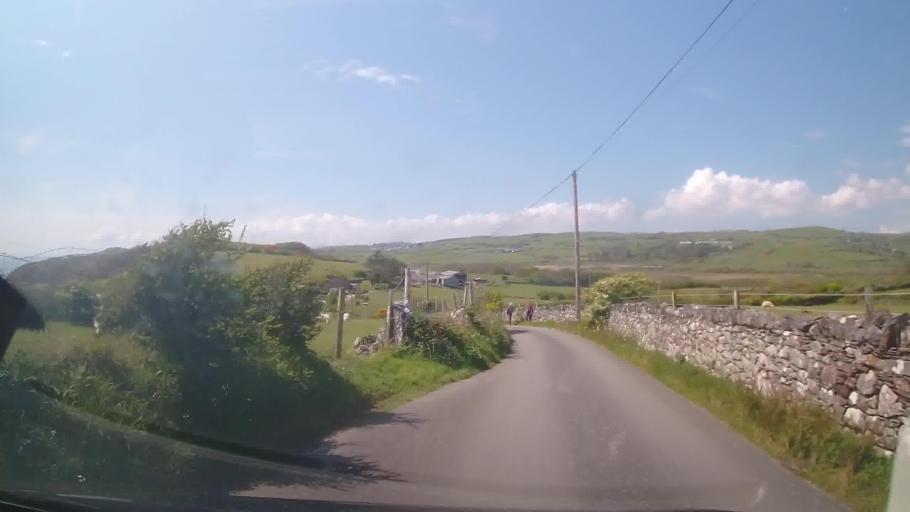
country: GB
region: Wales
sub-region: Gwynedd
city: Criccieth
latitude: 52.9183
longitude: -4.1852
